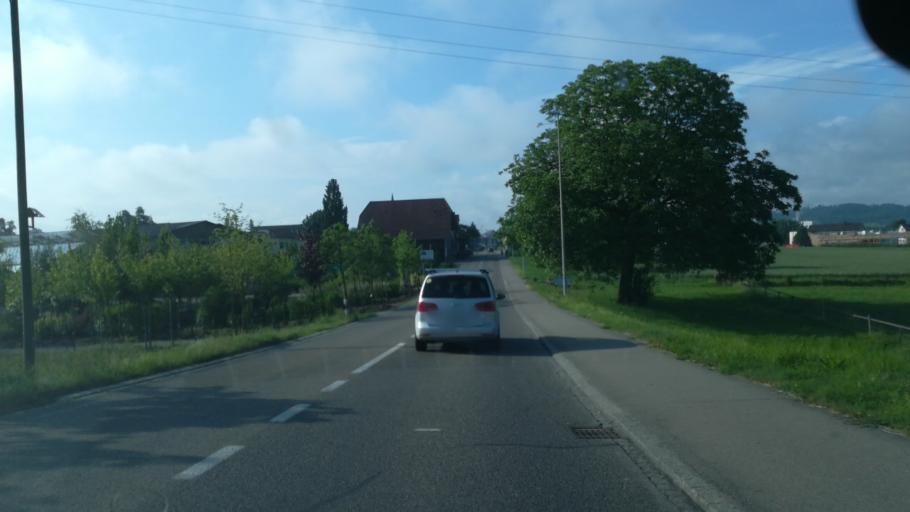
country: CH
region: Thurgau
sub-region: Weinfelden District
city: Sulgen
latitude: 47.5483
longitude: 9.1795
